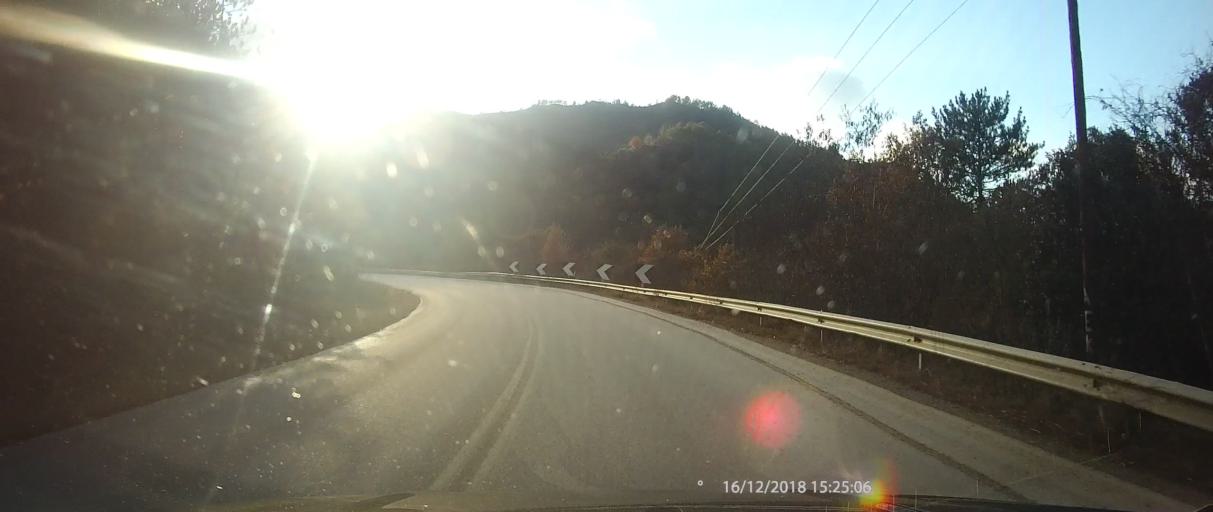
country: GR
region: Epirus
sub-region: Nomos Ioanninon
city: Konitsa
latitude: 40.1323
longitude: 20.7824
